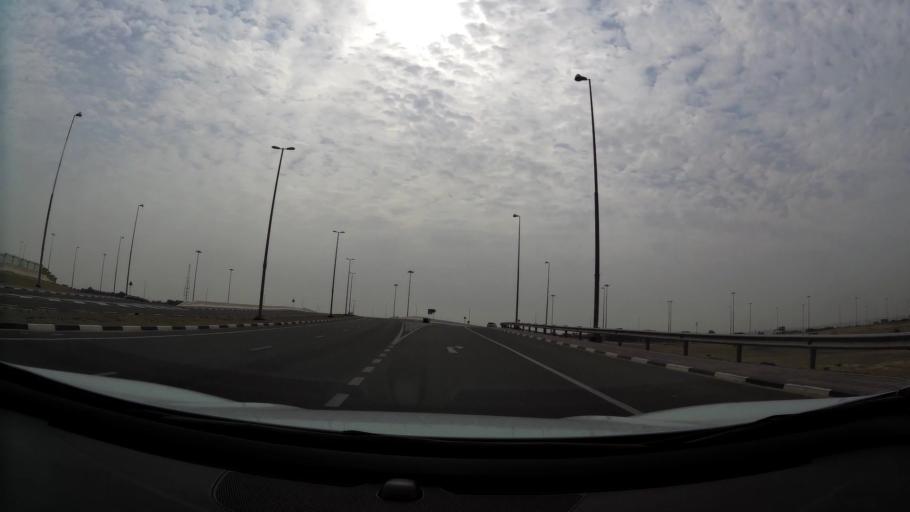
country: AE
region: Abu Dhabi
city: Abu Dhabi
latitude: 24.6871
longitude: 54.7712
